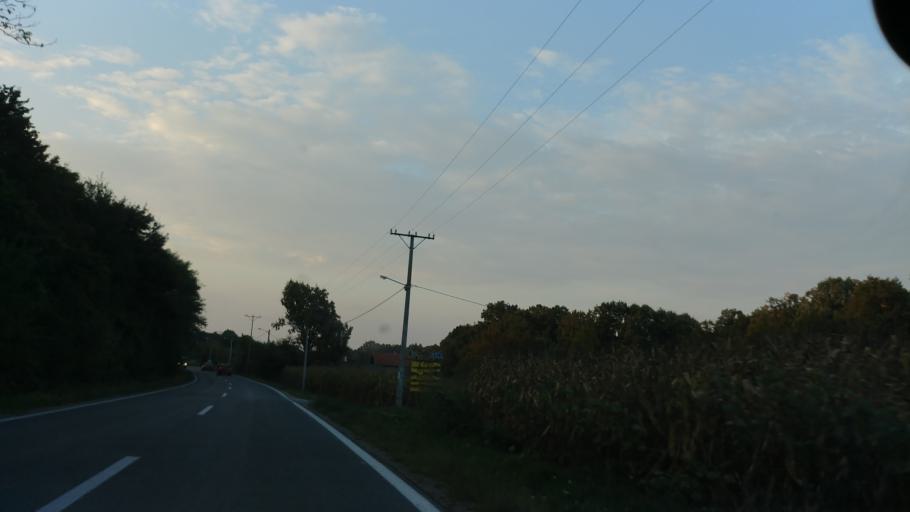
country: BA
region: Brcko
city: Brcko
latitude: 44.7894
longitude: 18.8167
